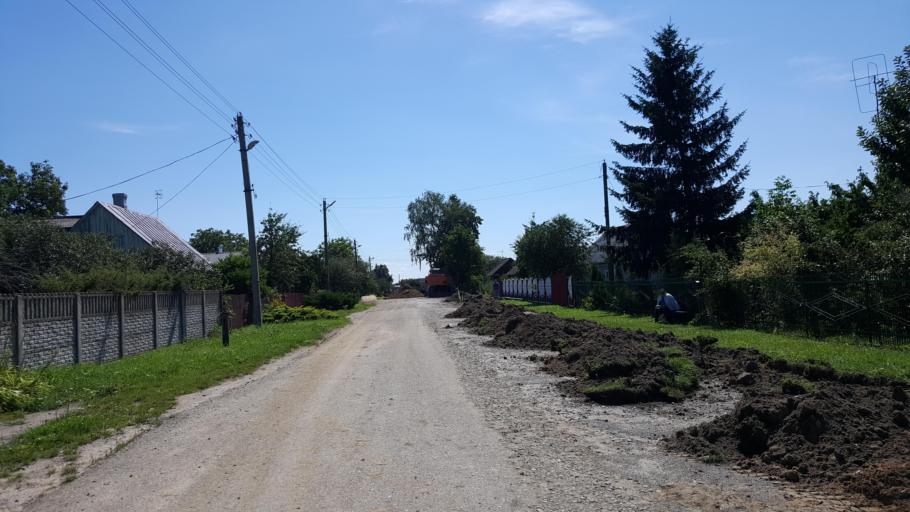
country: BY
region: Brest
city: Charnawchytsy
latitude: 52.2257
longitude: 23.7331
